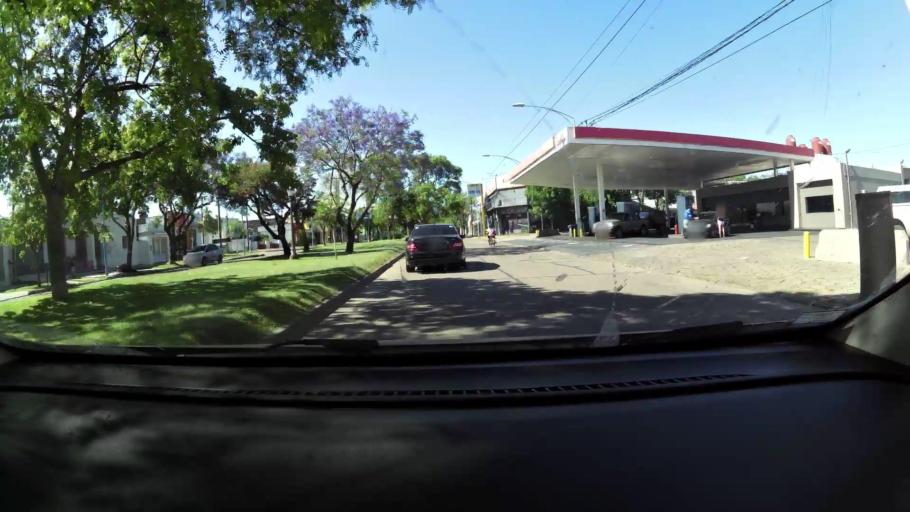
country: AR
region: Santa Fe
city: Rafaela
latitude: -31.2614
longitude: -61.4937
